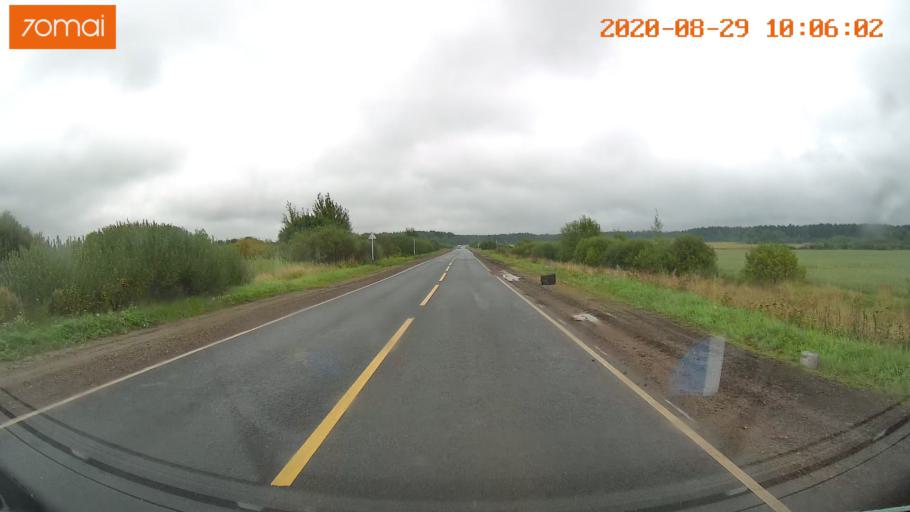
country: RU
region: Ivanovo
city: Zarechnyy
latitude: 57.3904
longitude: 42.5363
